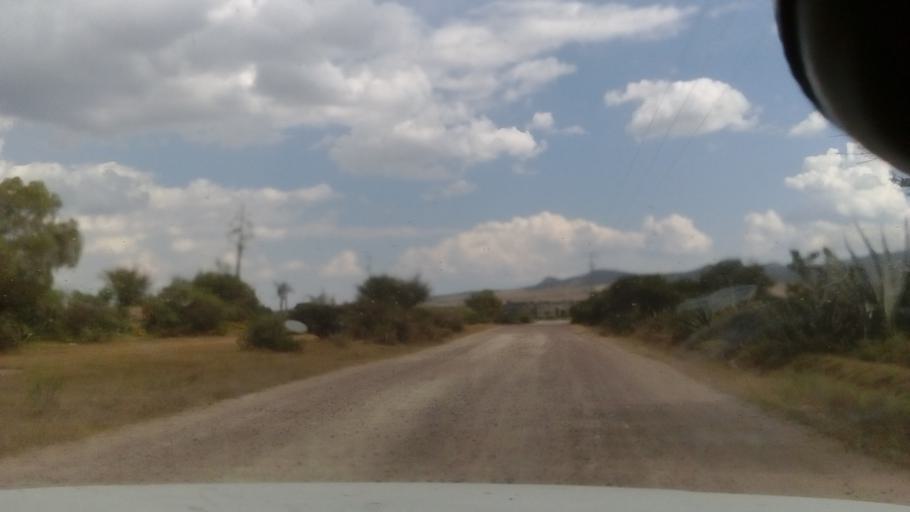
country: MX
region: Guanajuato
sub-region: Silao de la Victoria
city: San Francisco (Banos de Agua Caliente)
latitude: 21.2015
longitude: -101.4385
